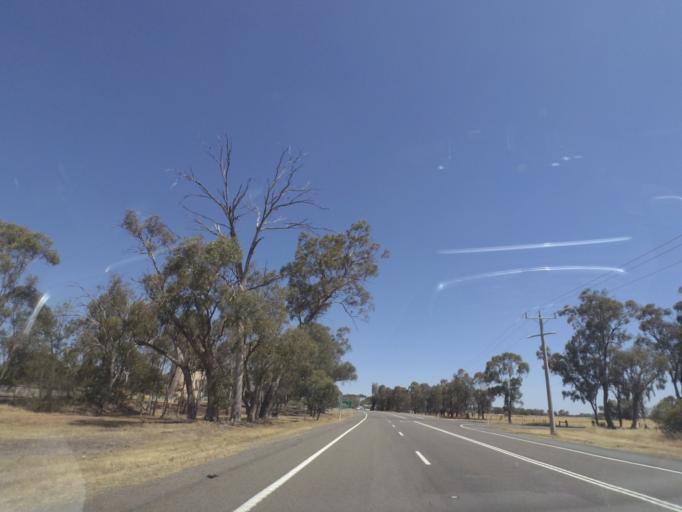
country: AU
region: Victoria
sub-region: Greater Shepparton
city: Shepparton
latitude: -36.2358
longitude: 145.4316
